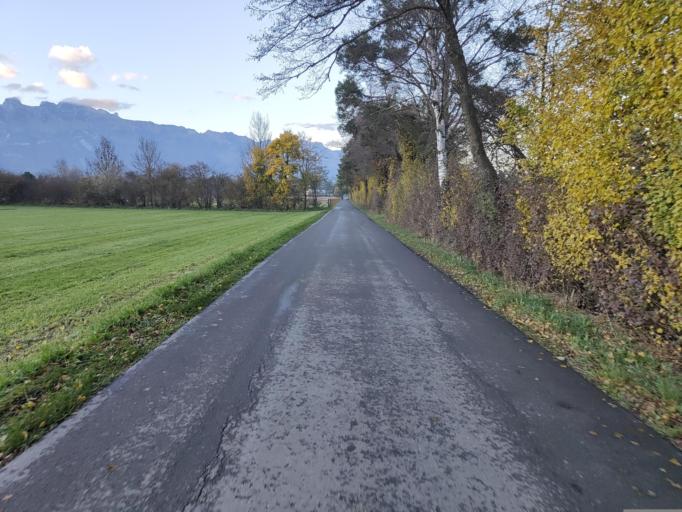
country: LI
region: Planken
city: Planken
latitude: 47.1879
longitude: 9.5254
